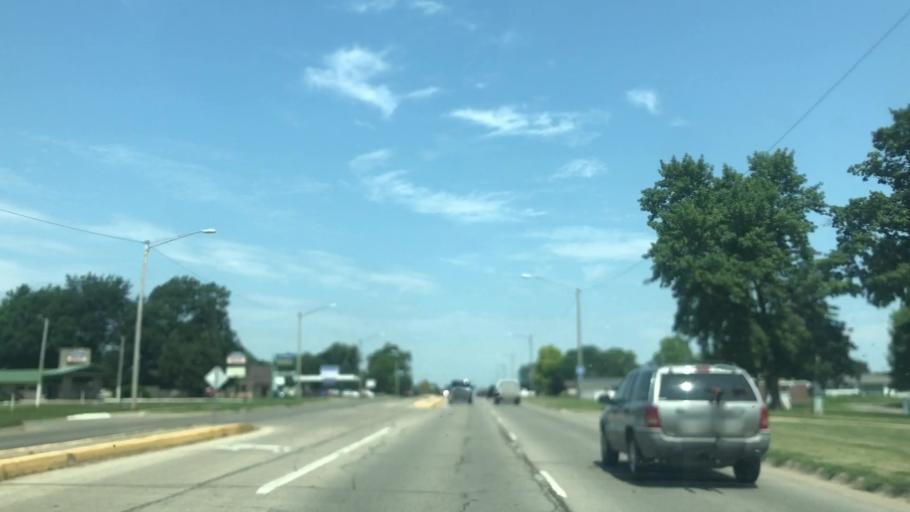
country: US
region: Iowa
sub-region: Marshall County
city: Marshalltown
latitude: 42.0217
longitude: -92.9124
